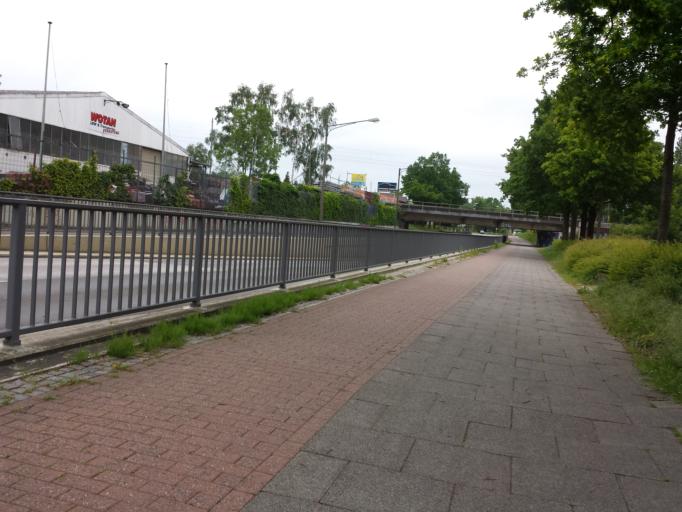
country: DE
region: Bremen
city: Bremen
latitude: 53.1023
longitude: 8.8153
